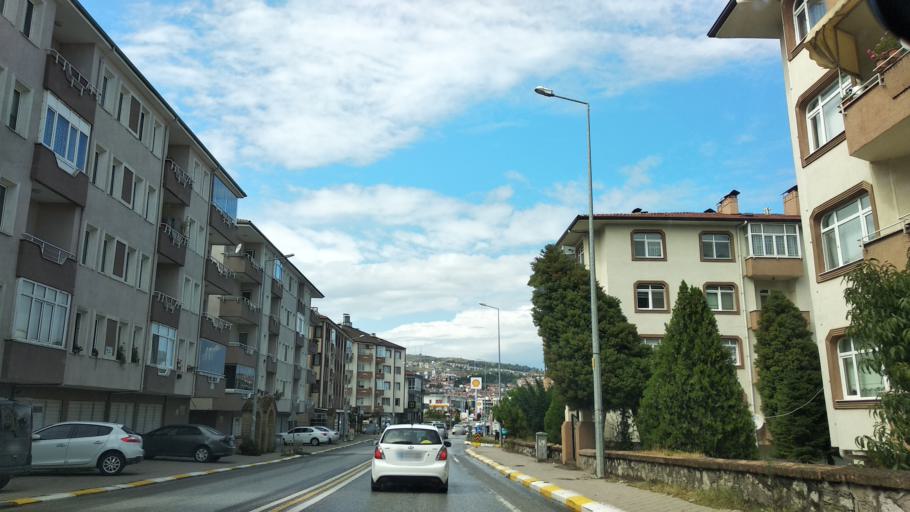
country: TR
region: Sakarya
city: Adapazari
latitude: 40.7581
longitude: 30.3685
